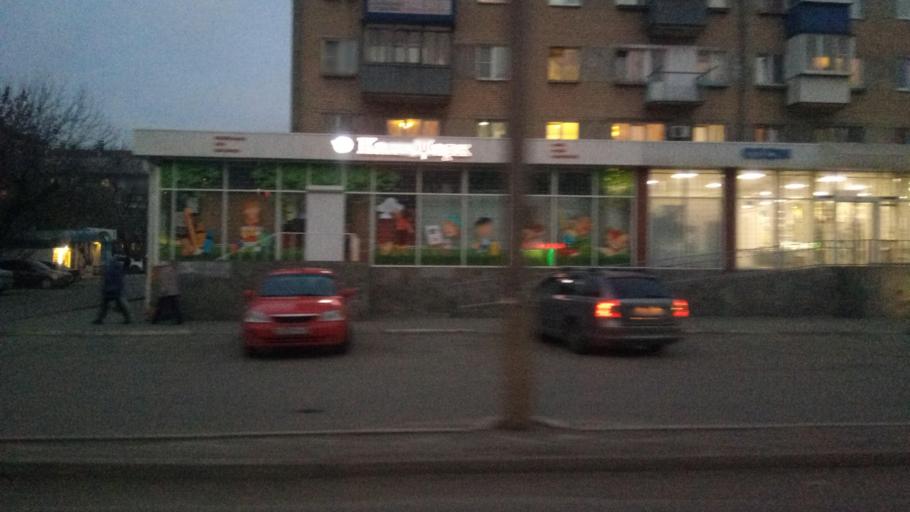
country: RU
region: Chelyabinsk
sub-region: Gorod Chelyabinsk
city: Chelyabinsk
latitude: 55.1711
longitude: 61.4630
